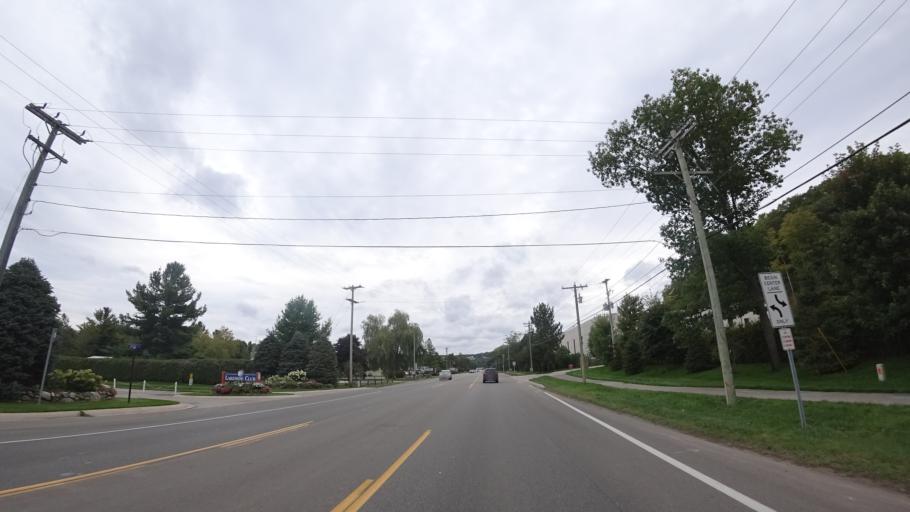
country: US
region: Michigan
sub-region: Emmet County
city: Petoskey
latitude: 45.4053
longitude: -84.9021
